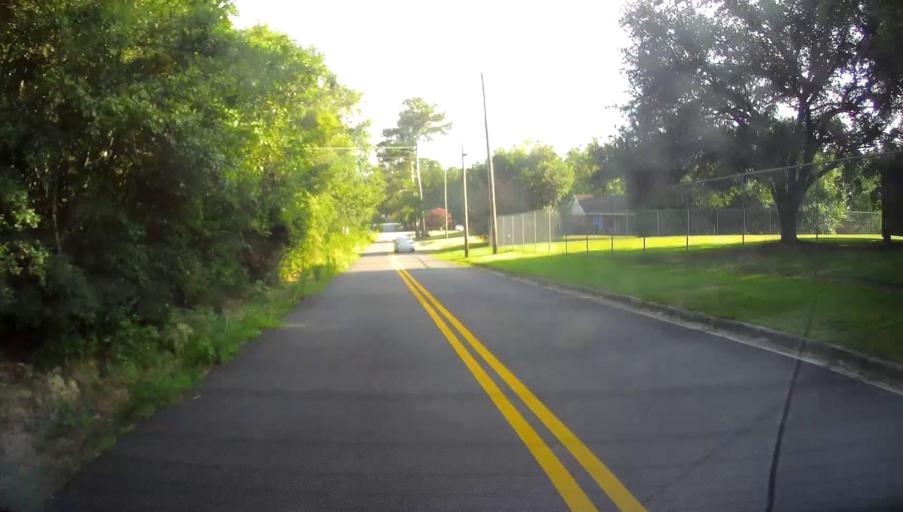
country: US
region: Georgia
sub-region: Crawford County
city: Roberta
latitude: 32.7230
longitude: -84.0163
